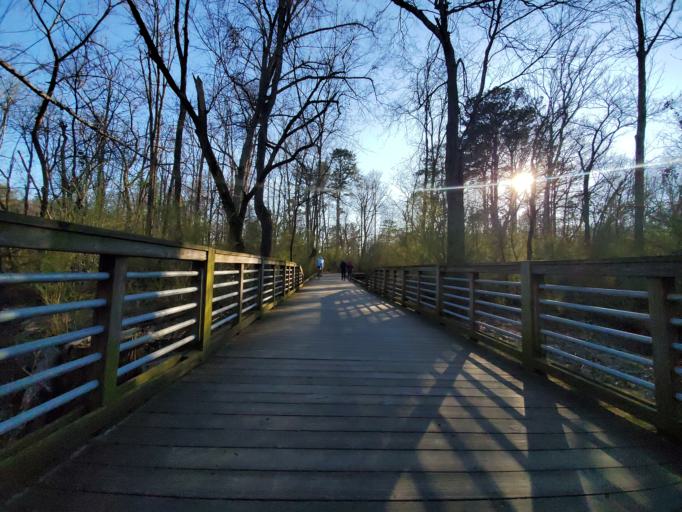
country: US
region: Georgia
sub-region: Gwinnett County
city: Lilburn
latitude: 33.8895
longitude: -84.1318
